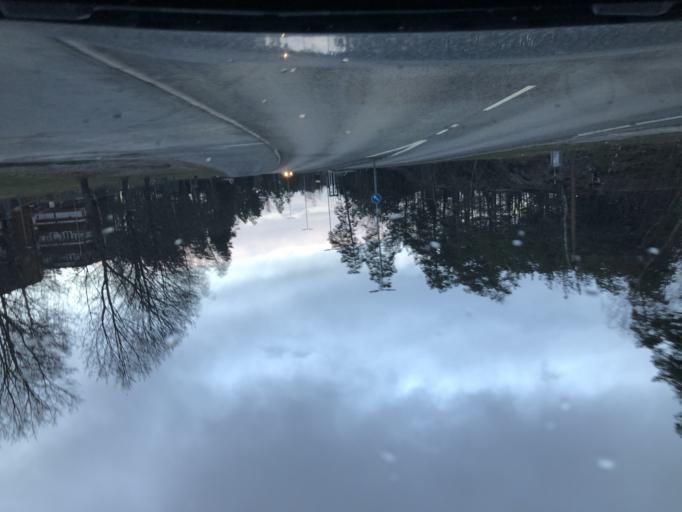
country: SE
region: Stockholm
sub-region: Sodertalje Kommun
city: Soedertaelje
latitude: 59.1784
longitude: 17.6084
